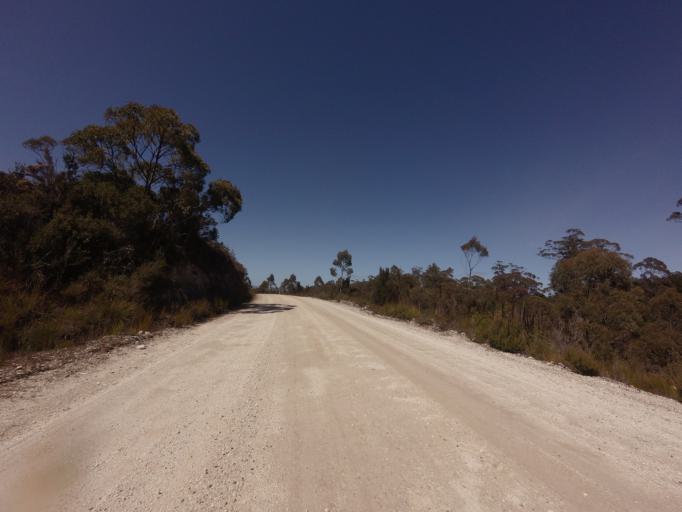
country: AU
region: Tasmania
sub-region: Huon Valley
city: Geeveston
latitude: -42.9411
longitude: 146.3480
